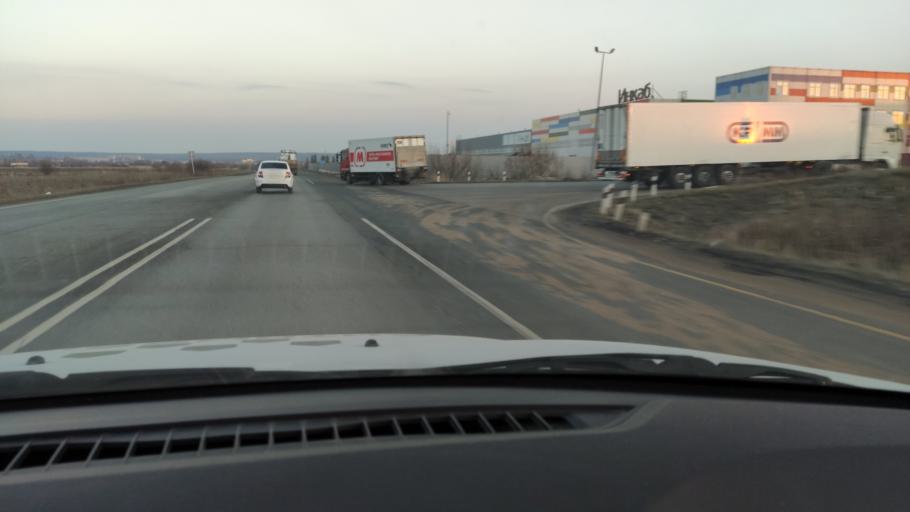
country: RU
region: Perm
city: Froly
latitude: 57.8968
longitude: 56.2472
